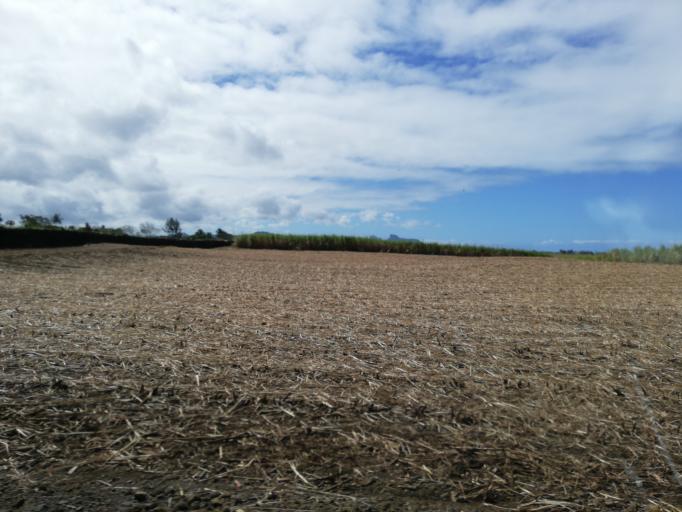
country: MU
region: Grand Port
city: Plaine Magnien
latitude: -20.4579
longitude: 57.6512
